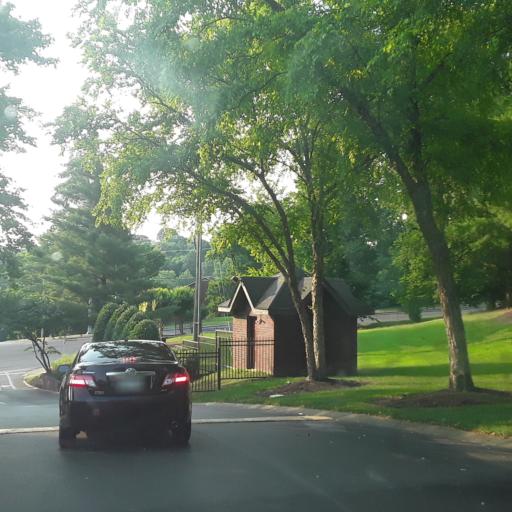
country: US
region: Tennessee
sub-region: Williamson County
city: Brentwood Estates
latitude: 36.0442
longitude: -86.7242
